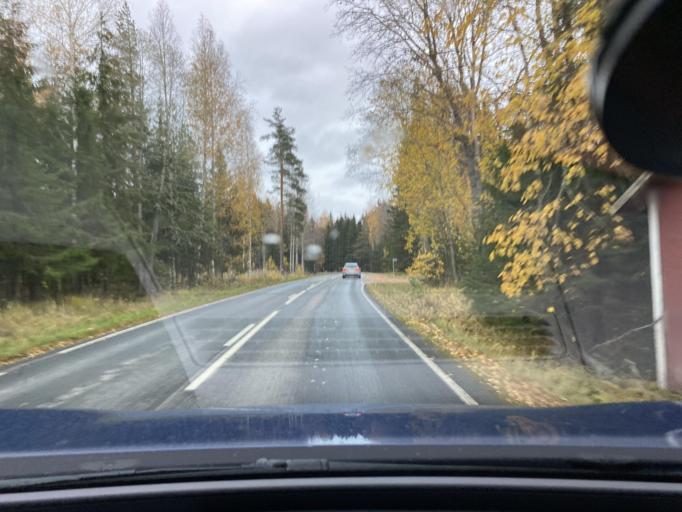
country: FI
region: Satakunta
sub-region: Pori
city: Huittinen
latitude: 61.1002
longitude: 22.5517
